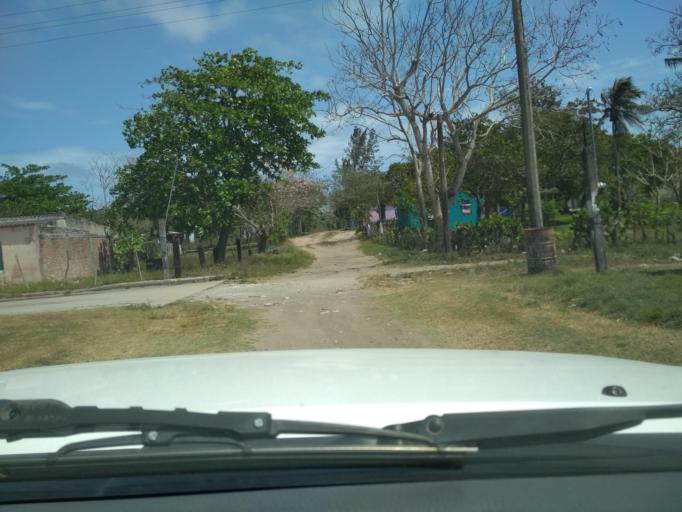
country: MX
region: Veracruz
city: Anton Lizardo
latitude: 19.0026
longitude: -95.9906
